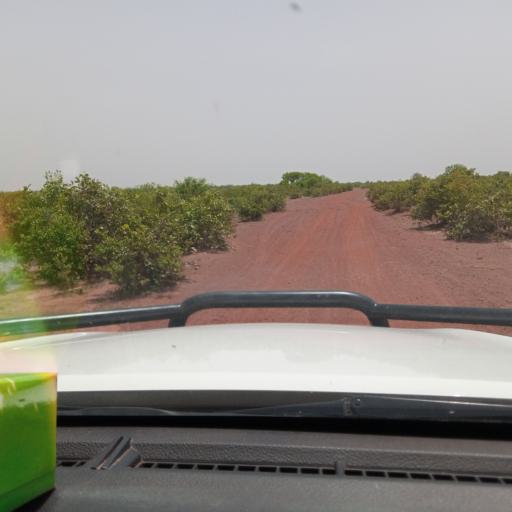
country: ML
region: Koulikoro
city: Koulikoro
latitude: 13.1091
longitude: -7.6150
